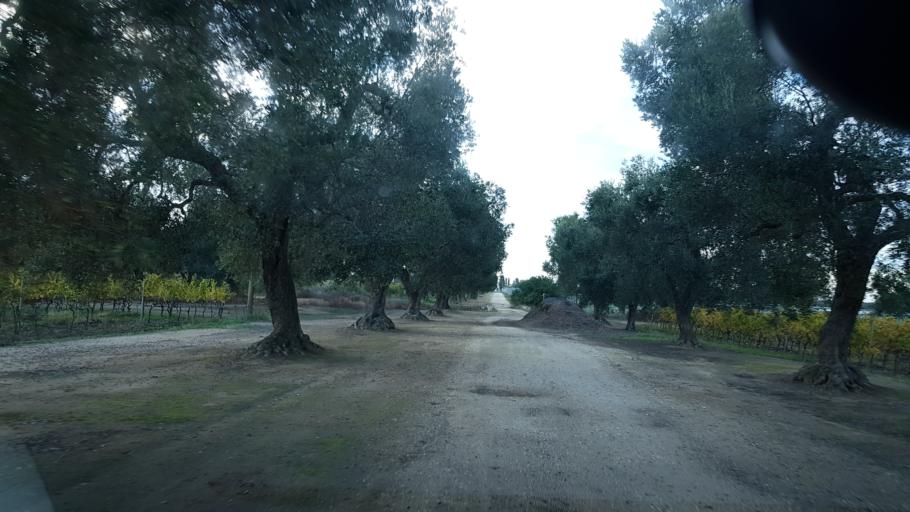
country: IT
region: Apulia
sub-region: Provincia di Brindisi
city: La Rosa
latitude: 40.5909
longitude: 17.9877
